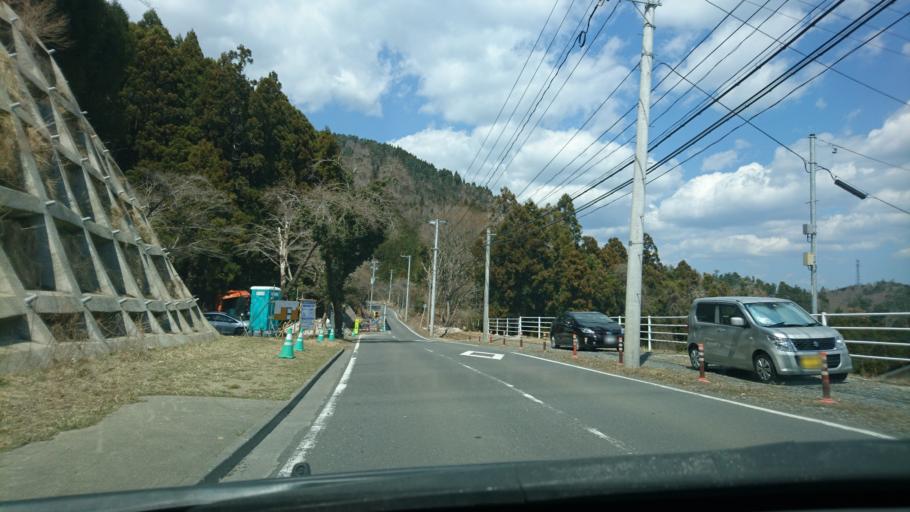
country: JP
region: Miyagi
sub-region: Oshika Gun
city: Onagawa Cho
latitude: 38.4410
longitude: 141.4846
